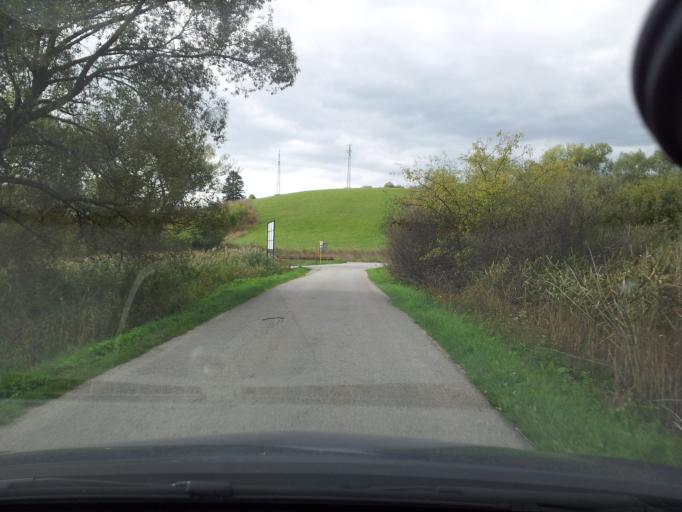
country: SK
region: Zilinsky
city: Ruzomberok
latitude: 49.1068
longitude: 19.4467
